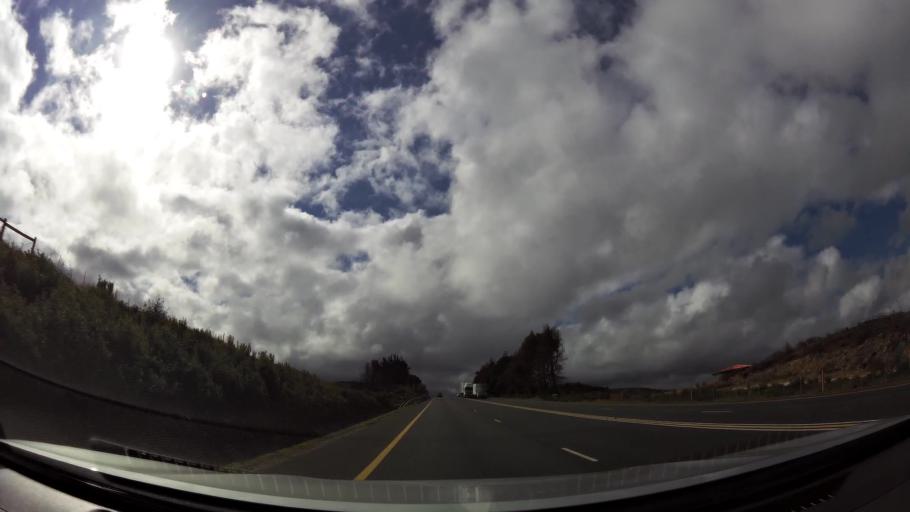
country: ZA
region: Western Cape
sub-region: Eden District Municipality
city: Knysna
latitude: -34.0388
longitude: 23.1208
